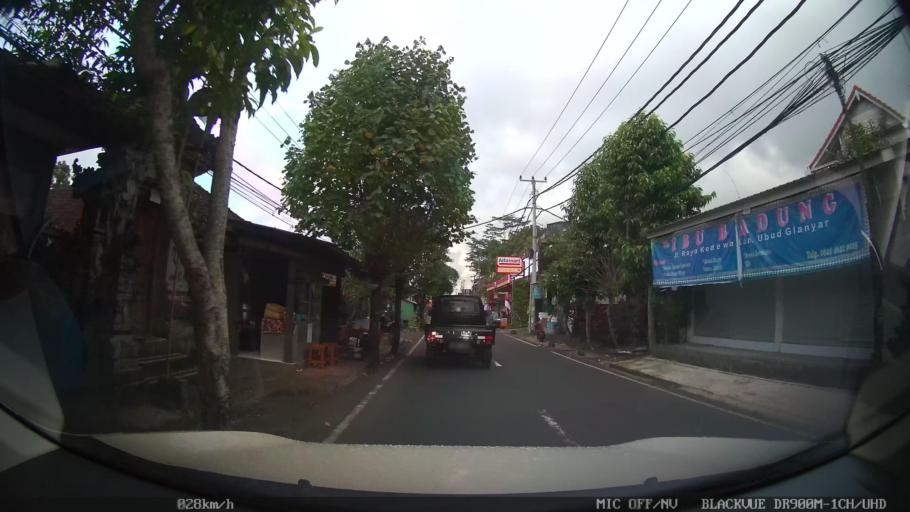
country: ID
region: Bali
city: Bunutan
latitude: -8.4790
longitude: 115.2479
